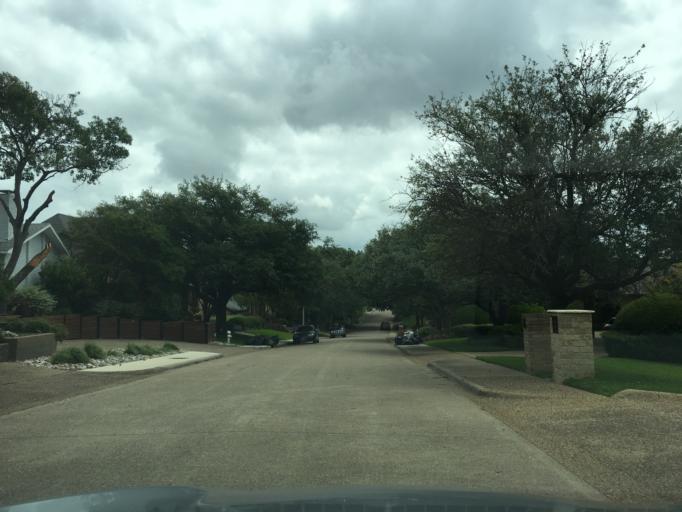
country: US
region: Texas
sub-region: Dallas County
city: Richardson
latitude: 32.8925
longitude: -96.7461
